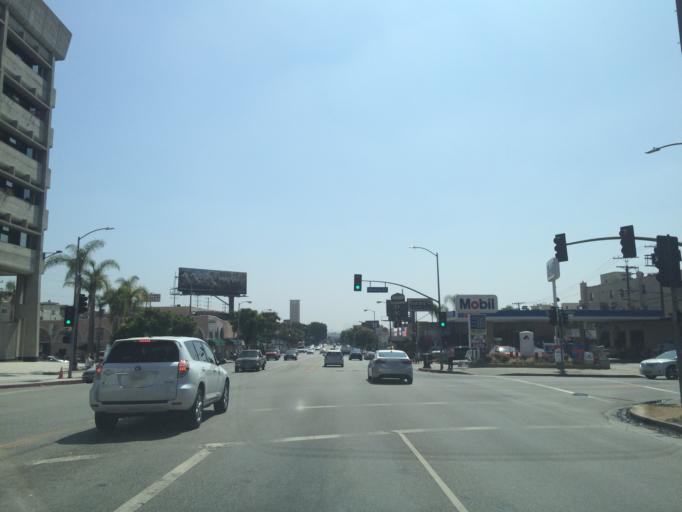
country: US
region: California
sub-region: Los Angeles County
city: Beverly Hills
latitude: 34.0553
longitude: -118.3958
